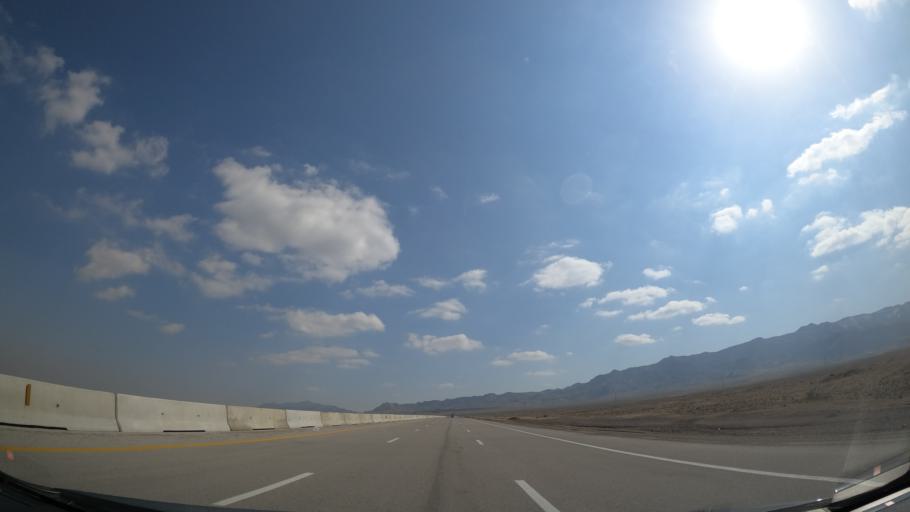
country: IR
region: Alborz
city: Eshtehard
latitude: 35.7233
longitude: 50.5666
